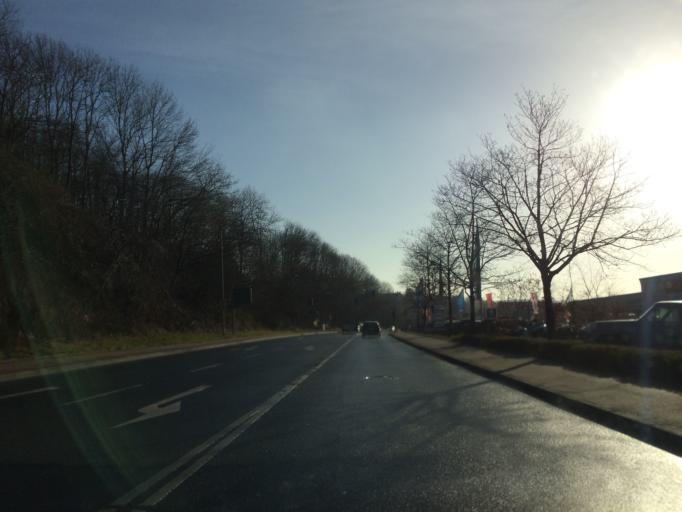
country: DE
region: North Rhine-Westphalia
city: Hattingen
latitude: 51.4085
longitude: 7.1936
